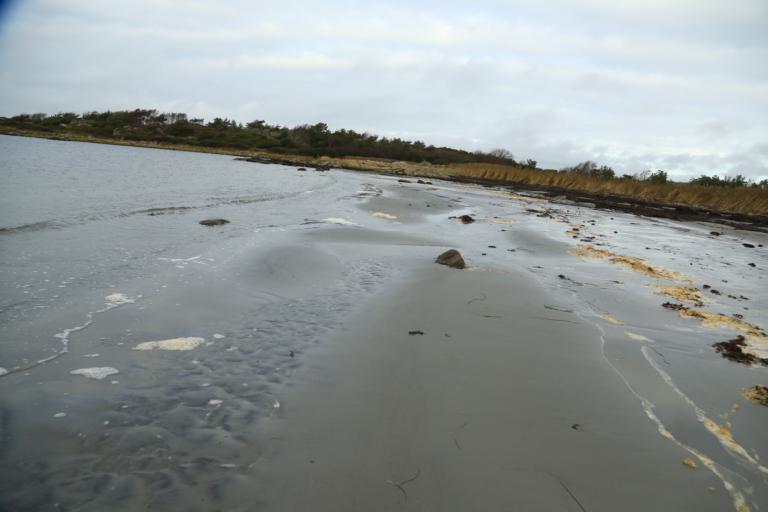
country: SE
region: Halland
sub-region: Varbergs Kommun
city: Varberg
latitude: 57.1764
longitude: 12.2053
